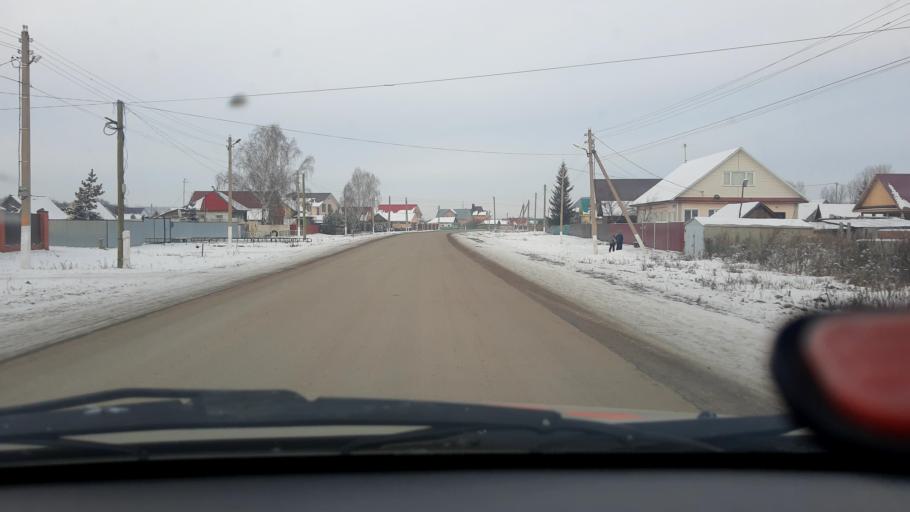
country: RU
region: Bashkortostan
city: Avdon
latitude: 54.4236
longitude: 55.8122
